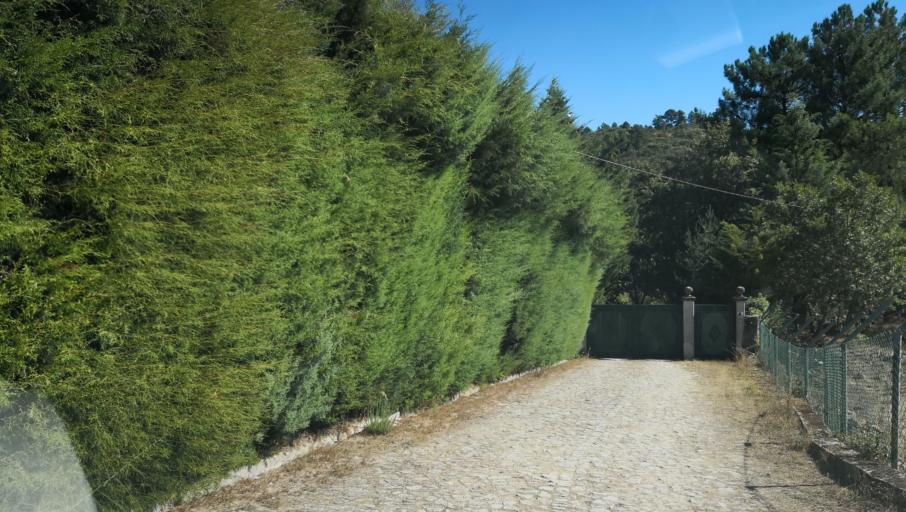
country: PT
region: Vila Real
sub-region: Vila Real
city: Vila Real
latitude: 41.3236
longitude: -7.7221
